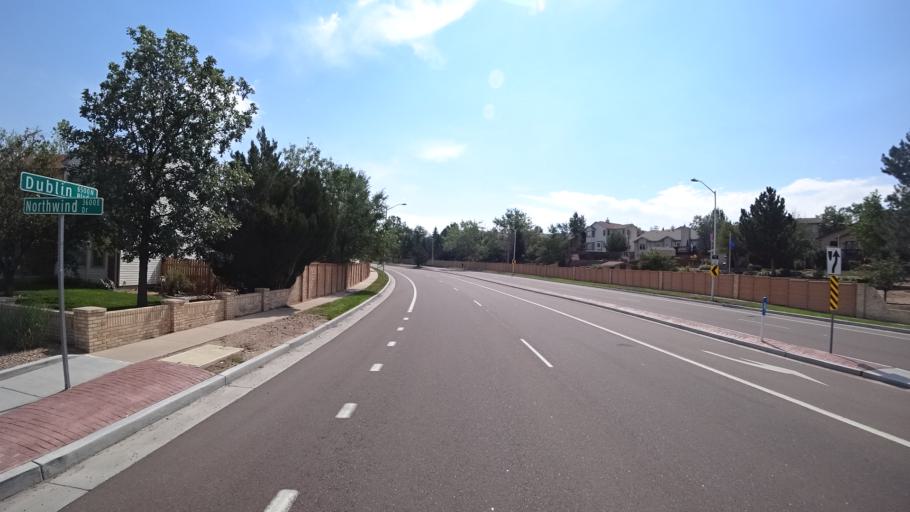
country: US
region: Colorado
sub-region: El Paso County
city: Cimarron Hills
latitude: 38.9247
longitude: -104.7606
